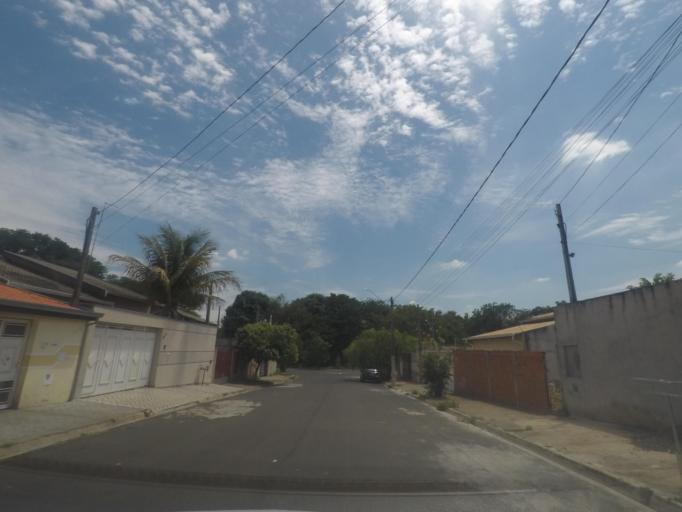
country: BR
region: Sao Paulo
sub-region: Sumare
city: Sumare
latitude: -22.7953
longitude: -47.2723
